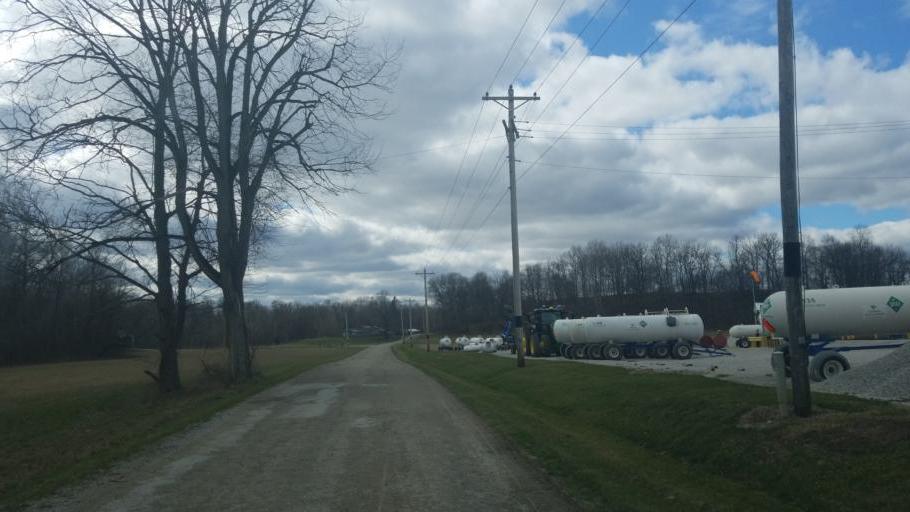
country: US
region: Indiana
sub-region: Parke County
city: Montezuma
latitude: 39.7741
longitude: -87.3202
